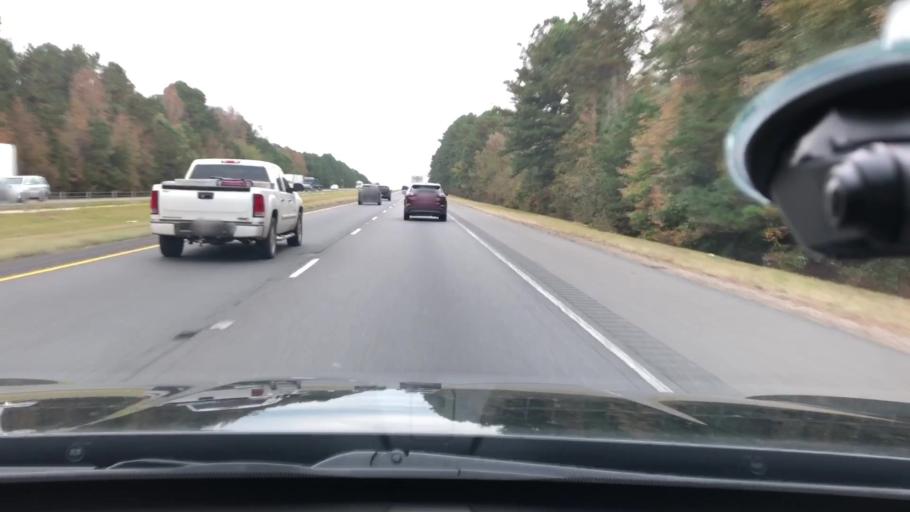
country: US
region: Arkansas
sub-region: Clark County
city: Arkadelphia
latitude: 34.0409
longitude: -93.1402
